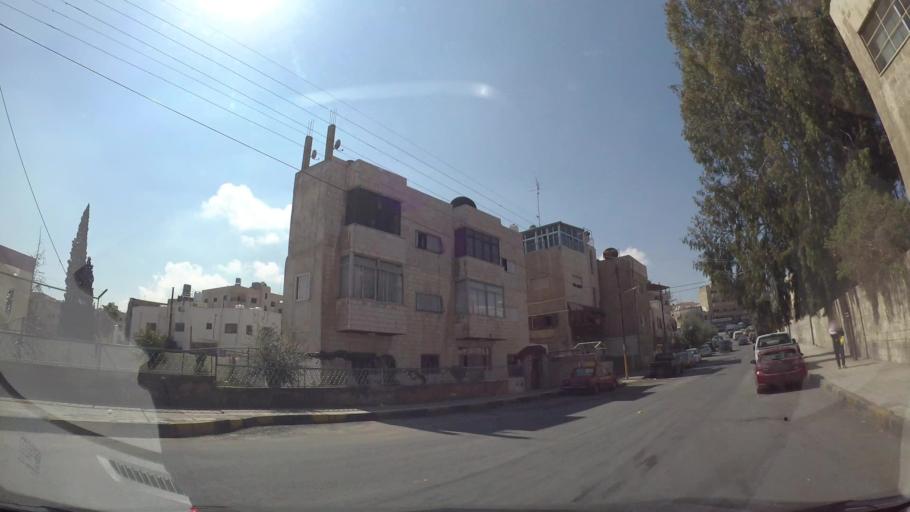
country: JO
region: Amman
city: Amman
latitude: 31.9788
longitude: 35.9868
